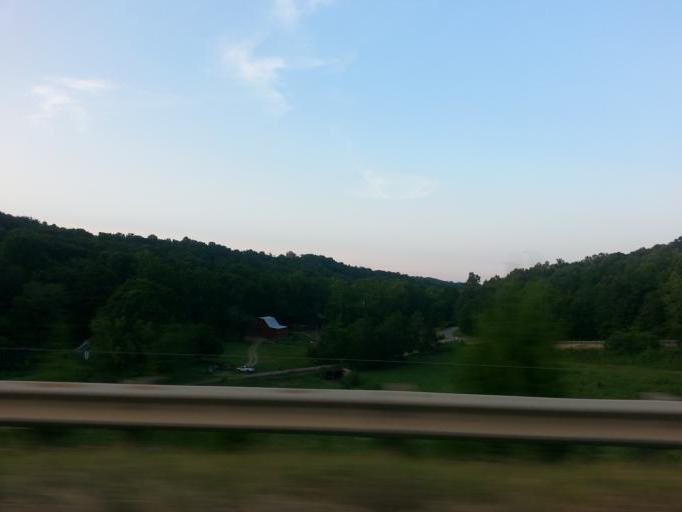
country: US
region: Tennessee
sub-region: Loudon County
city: Loudon
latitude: 35.7777
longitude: -84.3359
